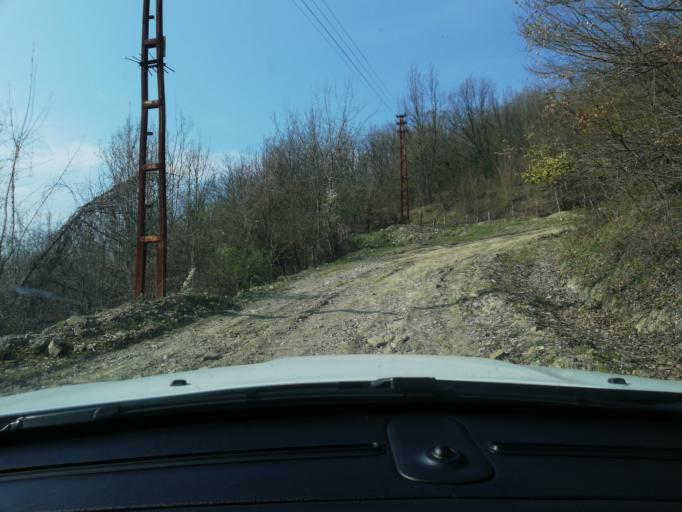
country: TR
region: Karabuk
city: Yenice
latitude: 41.2686
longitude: 32.3578
